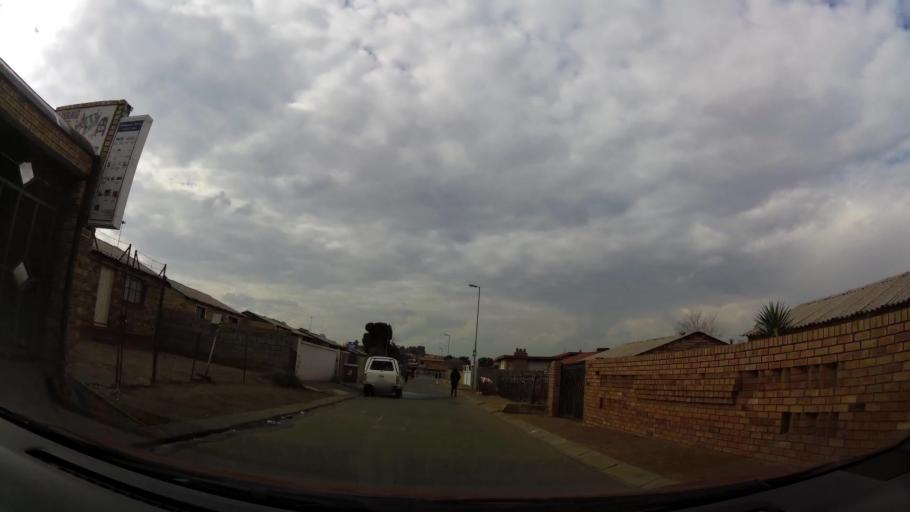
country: ZA
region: Gauteng
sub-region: City of Johannesburg Metropolitan Municipality
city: Soweto
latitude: -26.2383
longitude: 27.8617
